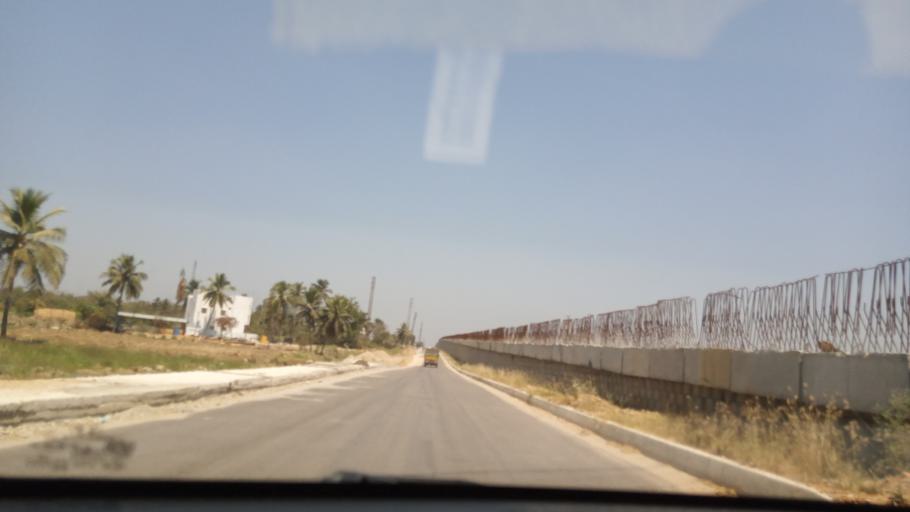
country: IN
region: Andhra Pradesh
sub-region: Chittoor
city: Pakala
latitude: 13.3513
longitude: 79.0840
